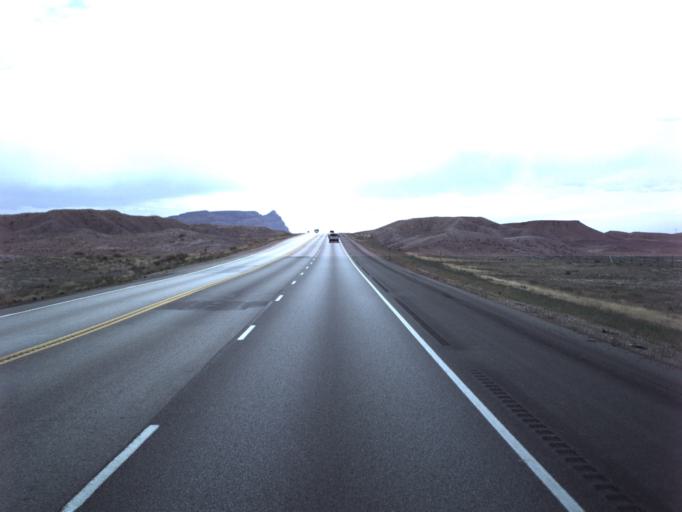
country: US
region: Utah
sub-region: Carbon County
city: East Carbon City
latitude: 39.3089
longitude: -110.3603
